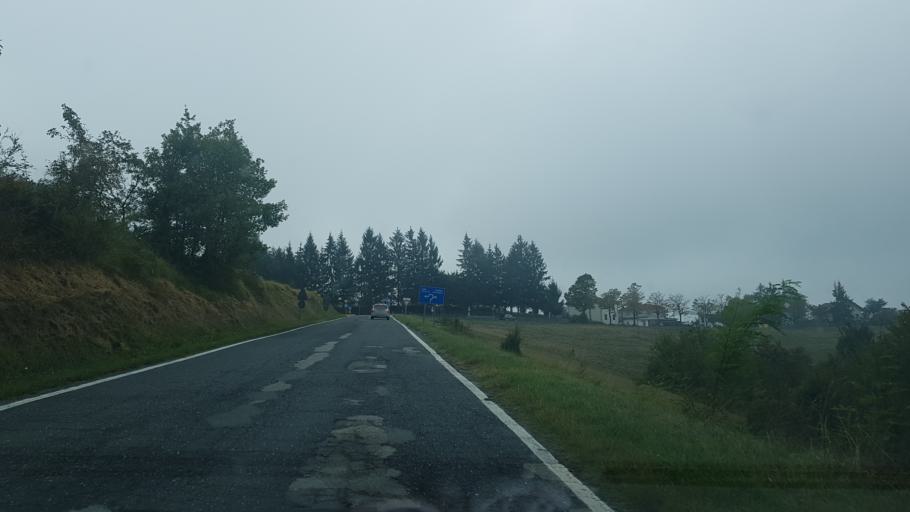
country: IT
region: Piedmont
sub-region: Provincia di Cuneo
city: Paroldo
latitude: 44.4264
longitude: 8.0947
